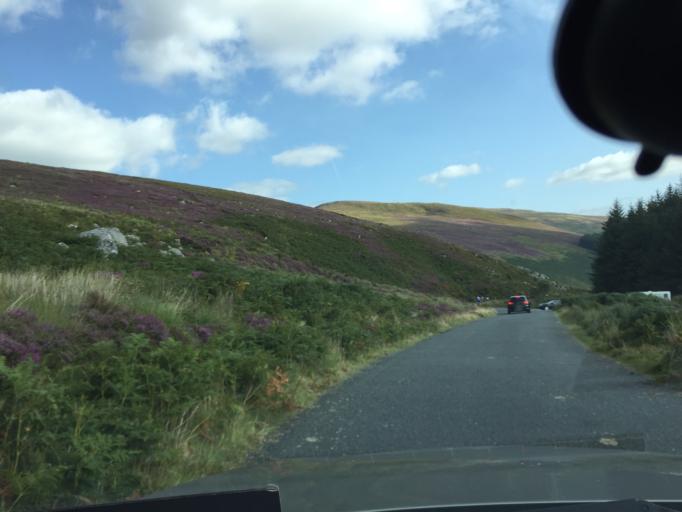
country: IE
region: Leinster
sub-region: Wicklow
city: Rathdrum
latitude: 53.0672
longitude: -6.3403
